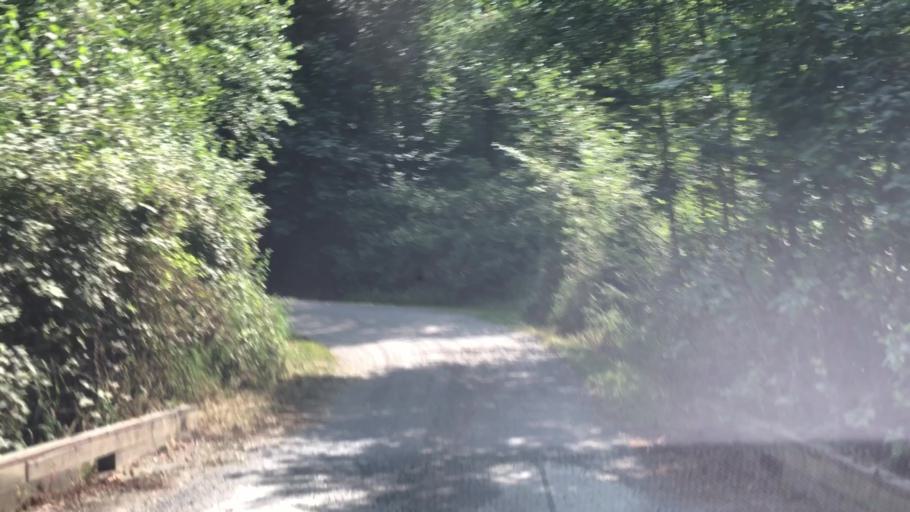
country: US
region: Washington
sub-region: Snohomish County
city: Lochsloy
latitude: 48.0510
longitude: -122.0232
